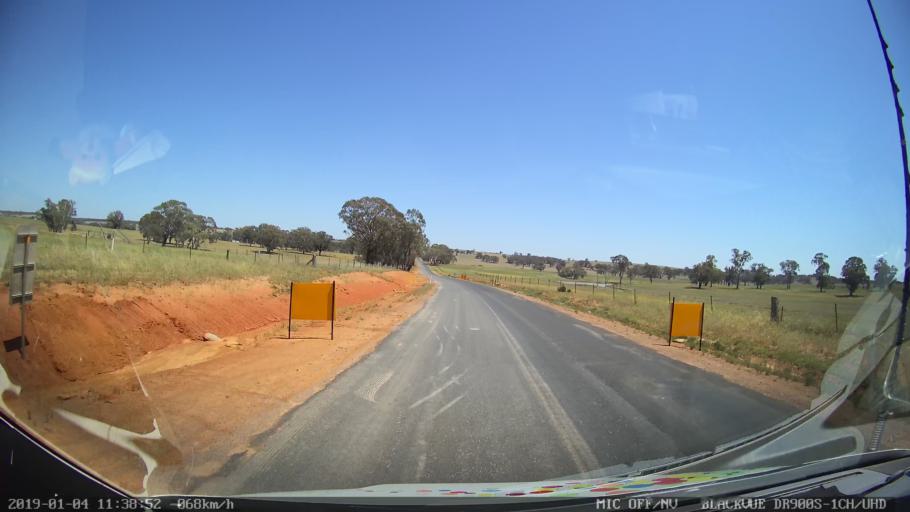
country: AU
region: New South Wales
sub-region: Cabonne
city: Molong
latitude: -33.0187
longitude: 148.8005
